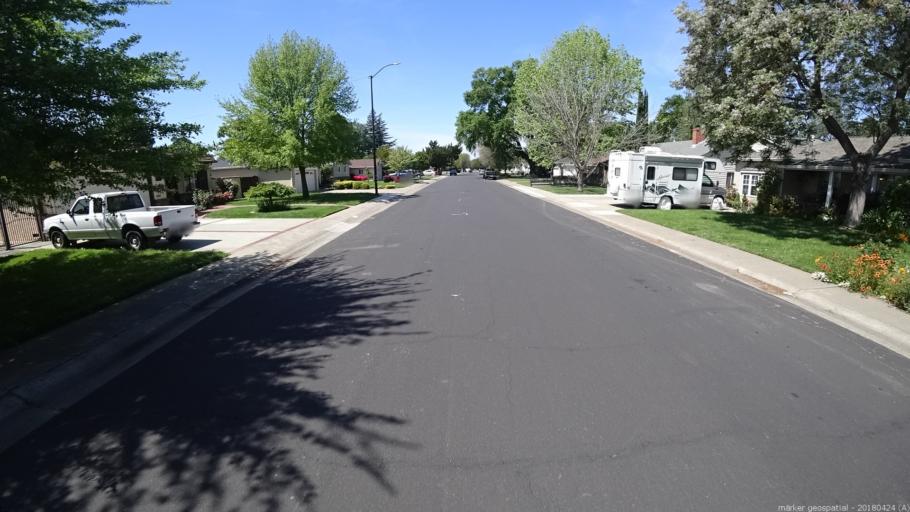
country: US
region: California
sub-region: Yolo County
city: West Sacramento
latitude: 38.5747
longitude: -121.5330
